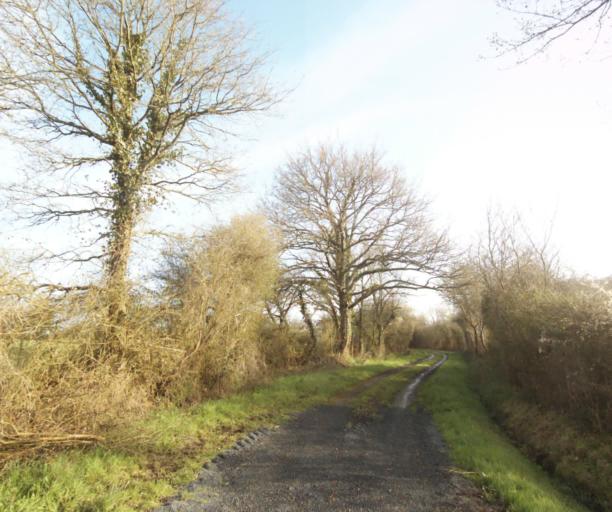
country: FR
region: Pays de la Loire
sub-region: Departement de la Loire-Atlantique
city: Malville
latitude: 47.3871
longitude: -1.8981
